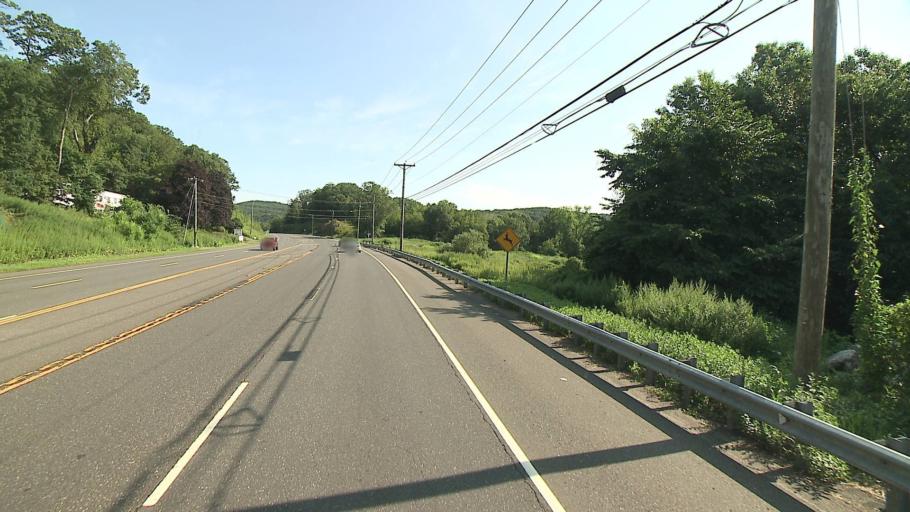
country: US
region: Connecticut
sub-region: Fairfield County
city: Danbury
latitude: 41.3374
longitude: -73.4704
